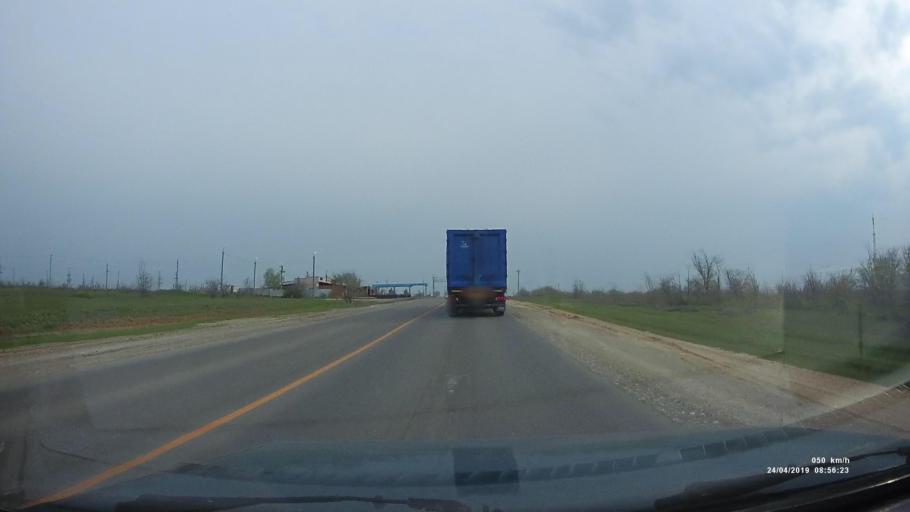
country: RU
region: Kalmykiya
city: Arshan'
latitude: 46.3010
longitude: 44.1845
